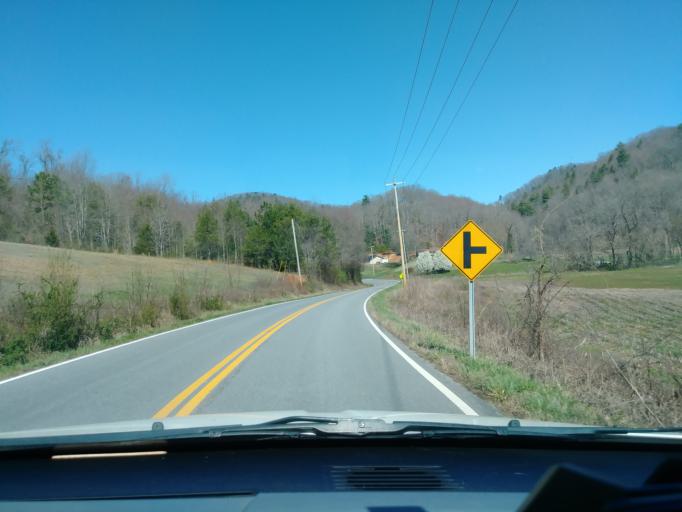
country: US
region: Tennessee
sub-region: Cocke County
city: Newport
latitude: 35.9629
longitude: -83.0488
